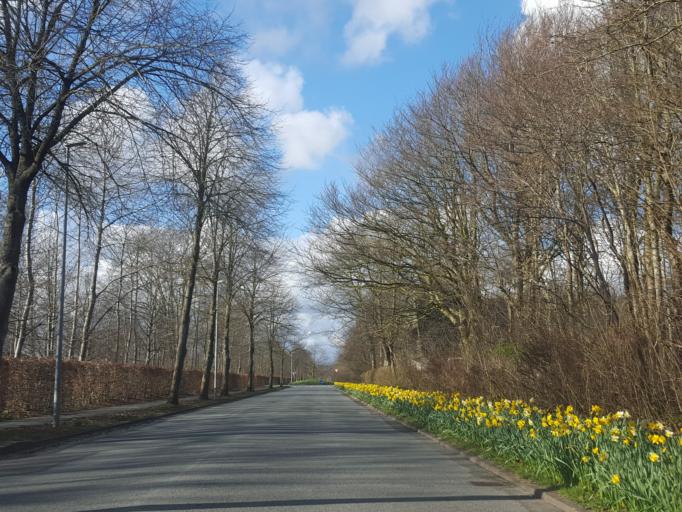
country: DK
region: South Denmark
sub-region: Esbjerg Kommune
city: Bramming
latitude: 55.4750
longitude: 8.7055
